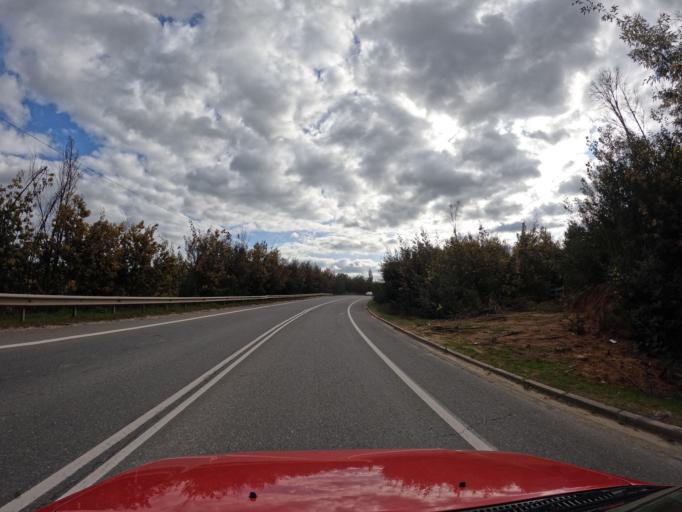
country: CL
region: Maule
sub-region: Provincia de Linares
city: San Javier
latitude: -35.5599
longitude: -72.0924
